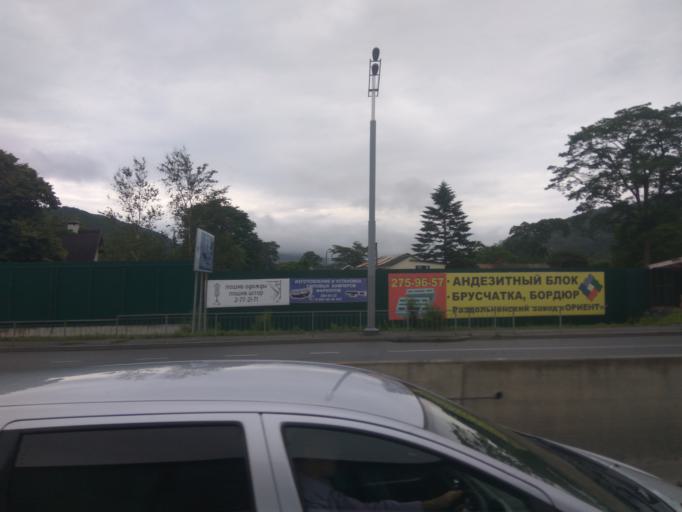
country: RU
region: Primorskiy
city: Trudovoye
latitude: 43.2176
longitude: 131.9599
